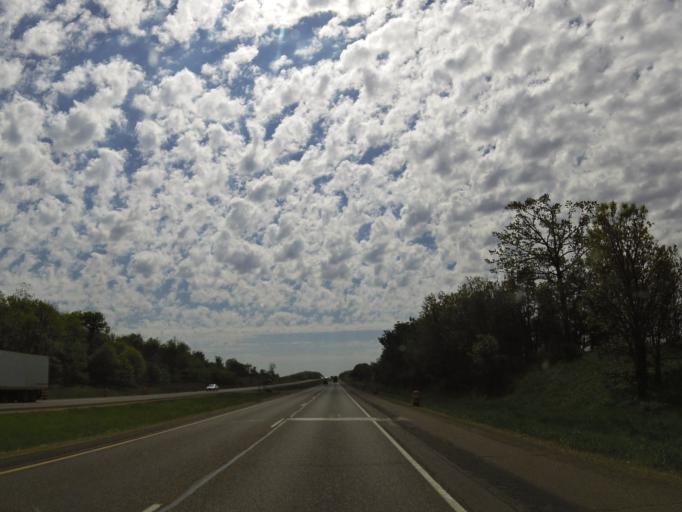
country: US
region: Wisconsin
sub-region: Dunn County
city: Colfax
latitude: 44.8911
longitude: -91.7412
